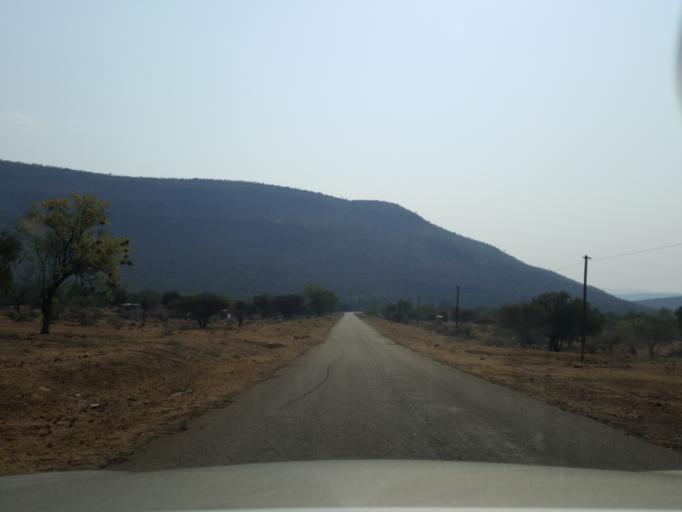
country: BW
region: South East
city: Lobatse
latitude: -25.3290
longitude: 25.7667
